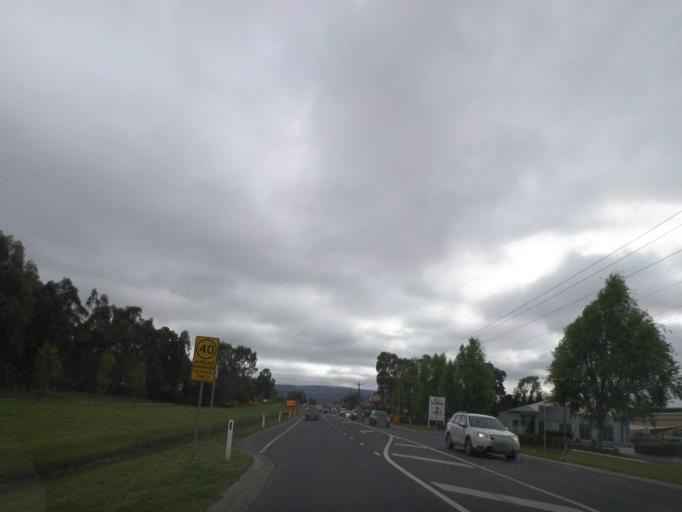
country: AU
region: Victoria
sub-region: Whittlesea
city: Whittlesea
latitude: -37.5177
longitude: 145.1140
